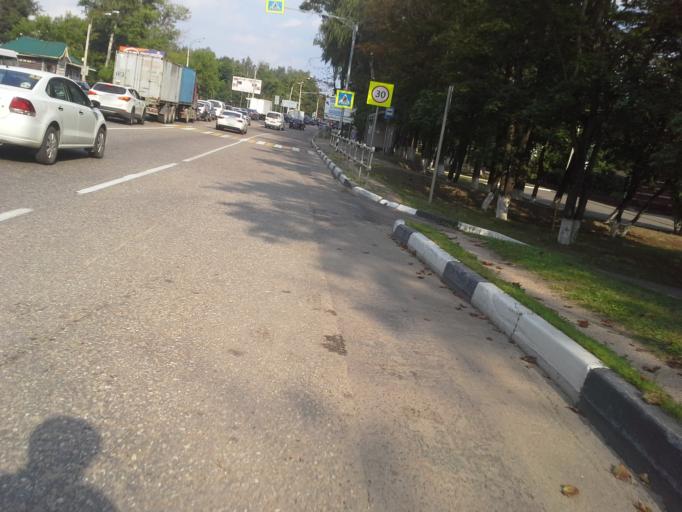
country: RU
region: Moskovskaya
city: Istra
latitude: 55.9207
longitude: 36.8555
